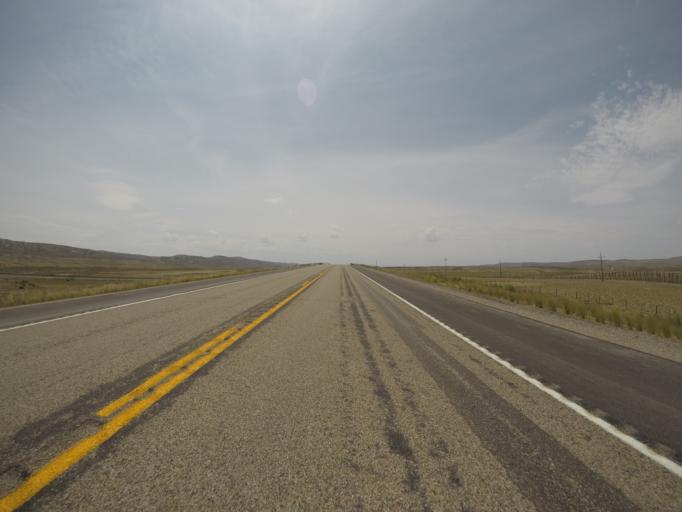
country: US
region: Wyoming
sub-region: Lincoln County
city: Kemmerer
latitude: 41.7096
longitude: -110.5657
